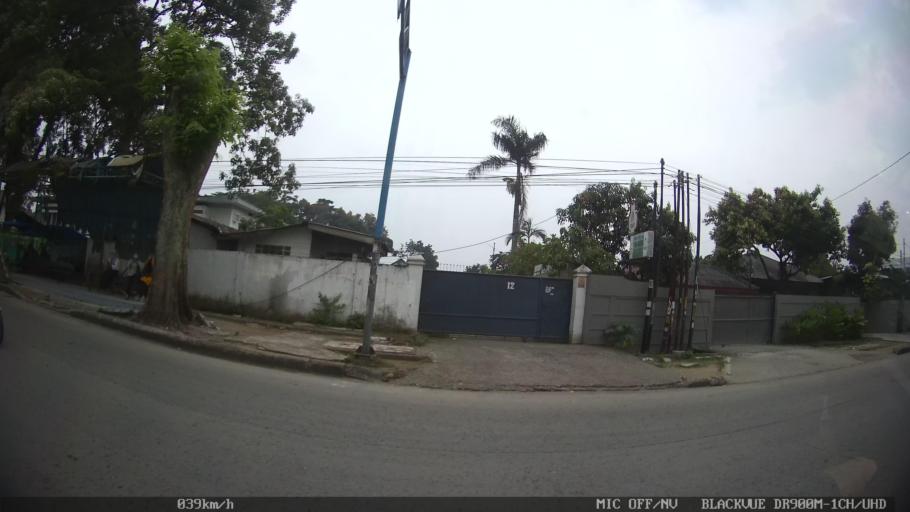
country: ID
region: North Sumatra
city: Deli Tua
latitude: 3.5434
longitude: 98.6985
